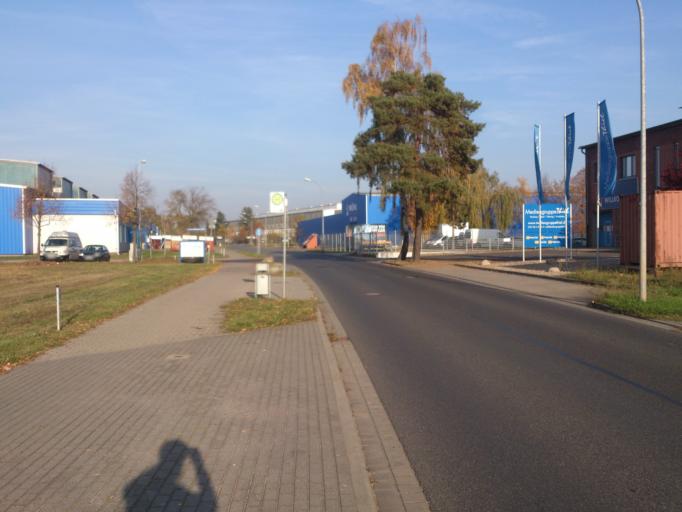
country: DE
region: Brandenburg
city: Ludwigsfelde
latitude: 52.3192
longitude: 13.2553
